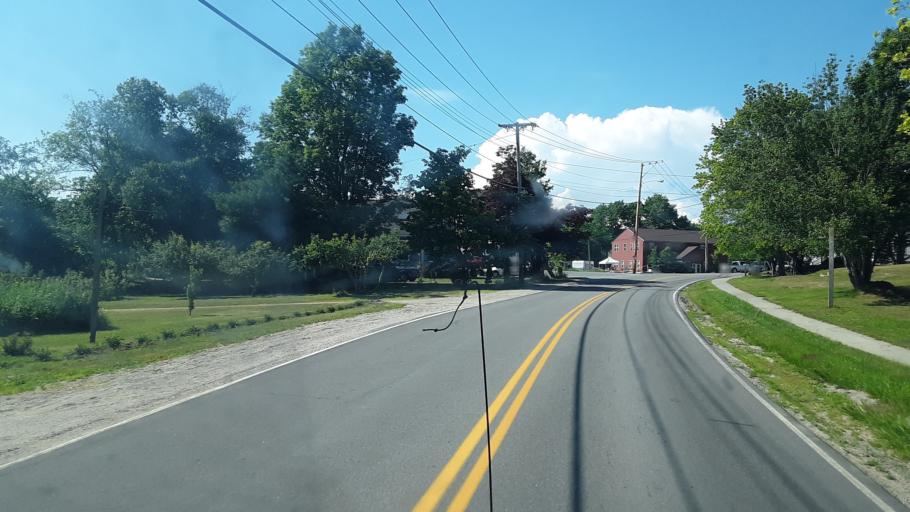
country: US
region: Maine
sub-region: Washington County
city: Cherryfield
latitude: 44.6062
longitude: -67.9263
